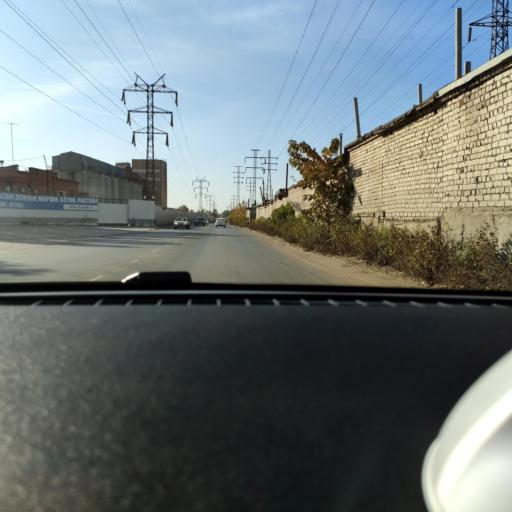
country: RU
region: Samara
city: Petra-Dubrava
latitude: 53.2497
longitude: 50.2940
